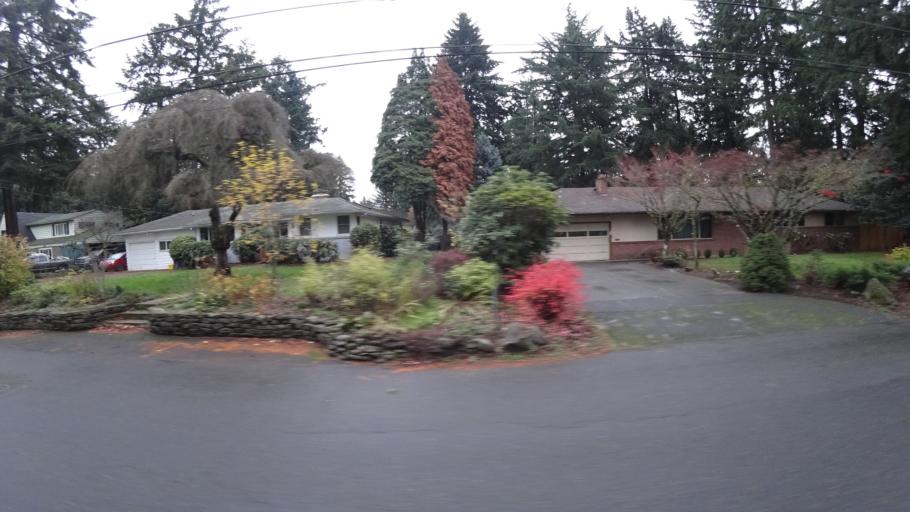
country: US
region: Oregon
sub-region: Multnomah County
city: Lents
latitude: 45.5295
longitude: -122.5484
